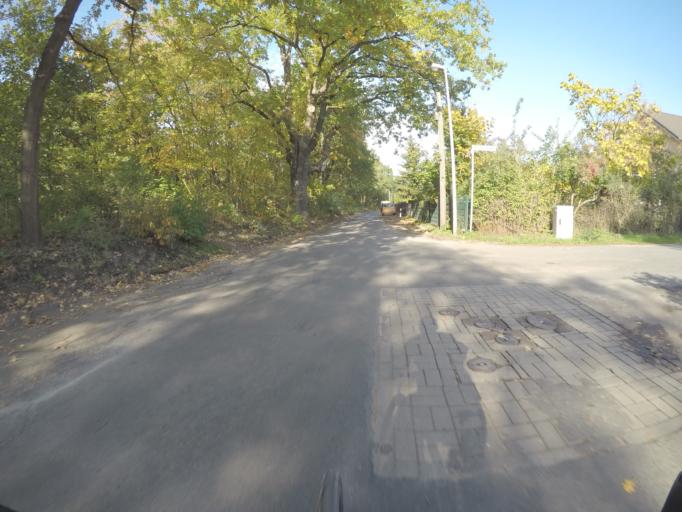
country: DE
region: Brandenburg
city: Oranienburg
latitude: 52.7368
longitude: 13.2254
